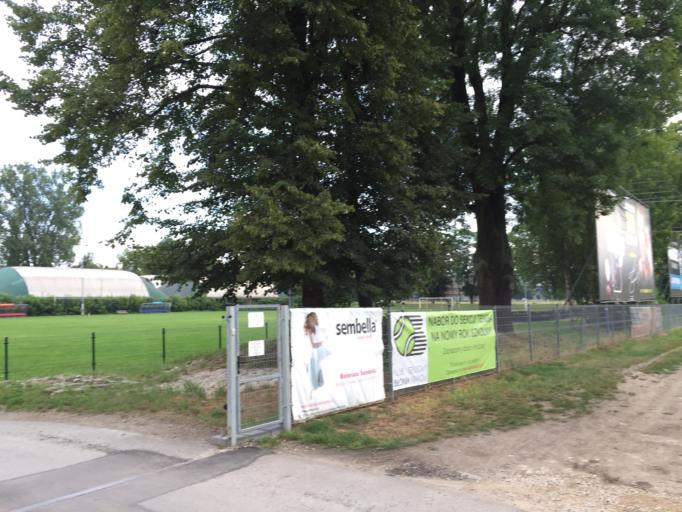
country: PL
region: Lesser Poland Voivodeship
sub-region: Krakow
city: Krakow
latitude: 50.0572
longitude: 19.9078
